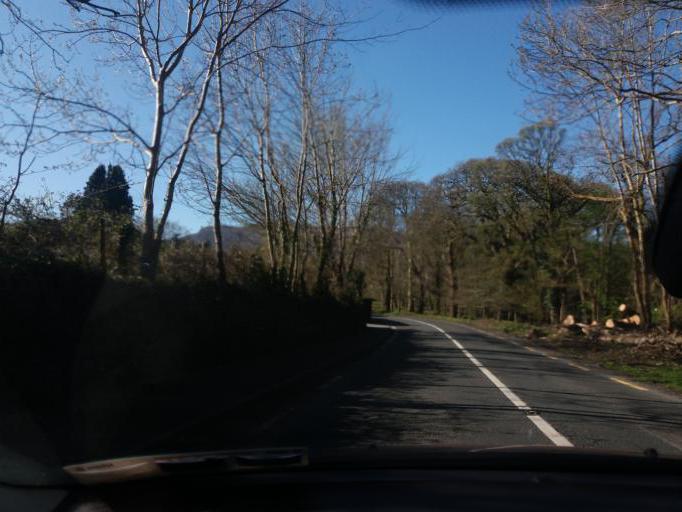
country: IE
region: Munster
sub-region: Ciarrai
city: Cill Airne
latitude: 52.0284
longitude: -9.4884
